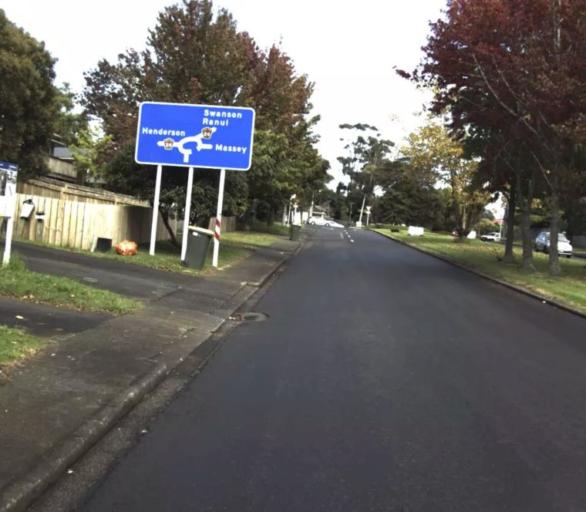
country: NZ
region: Auckland
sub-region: Auckland
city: Rosebank
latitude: -36.8600
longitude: 174.6131
